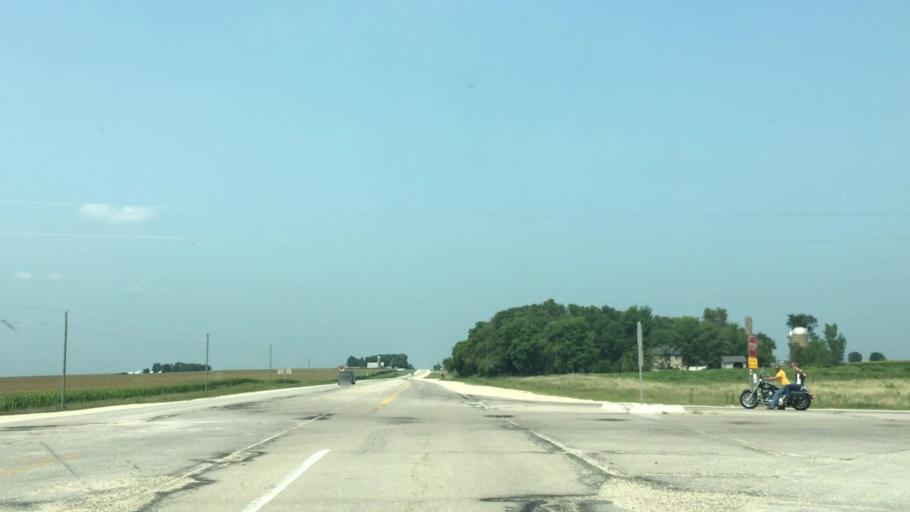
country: US
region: Iowa
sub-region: Fayette County
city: Fayette
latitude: 42.7599
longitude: -91.8044
